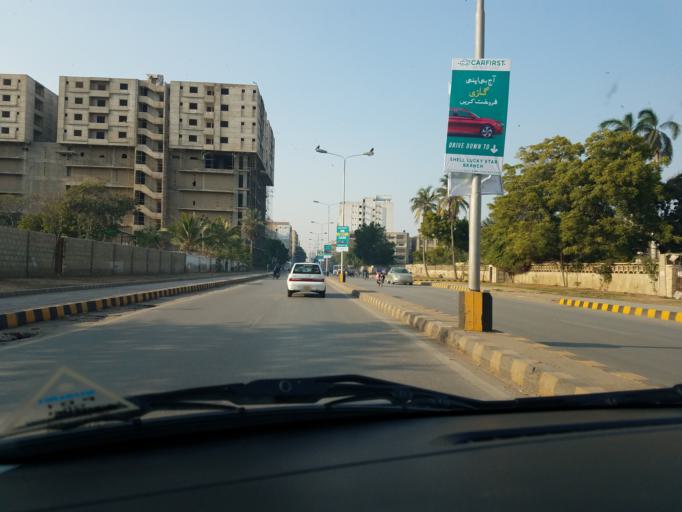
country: PK
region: Sindh
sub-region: Karachi District
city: Karachi
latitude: 24.8549
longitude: 67.0329
